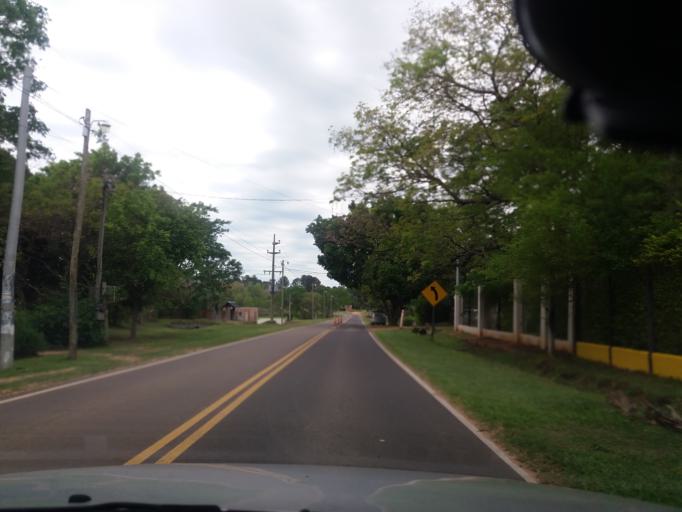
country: AR
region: Corrientes
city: San Luis del Palmar
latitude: -27.4594
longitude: -58.6684
